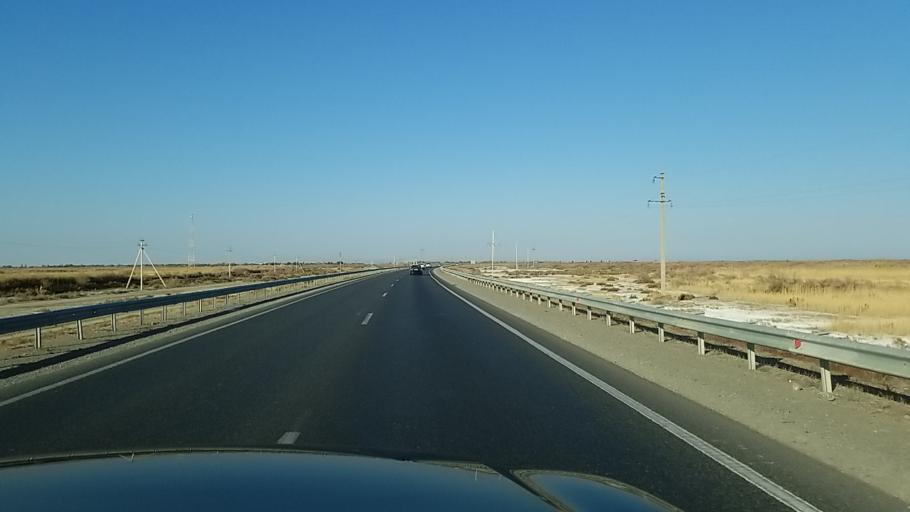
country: KZ
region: Qyzylorda
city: Terenozek
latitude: 44.8943
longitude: 65.0128
